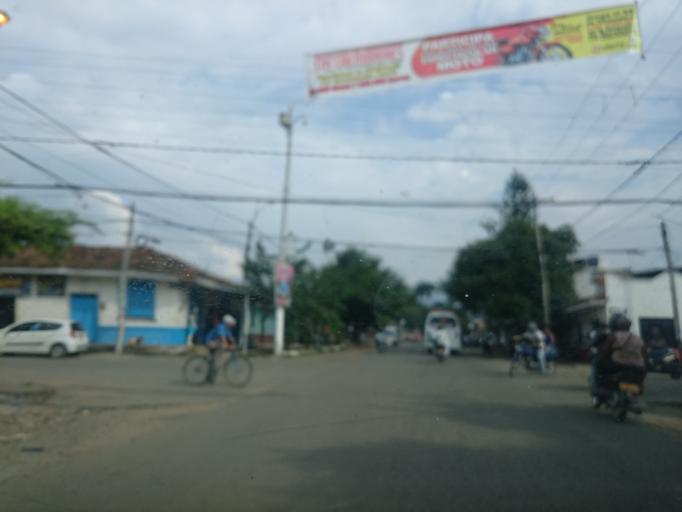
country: CO
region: Cauca
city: Santander de Quilichao
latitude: 3.0105
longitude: -76.4879
